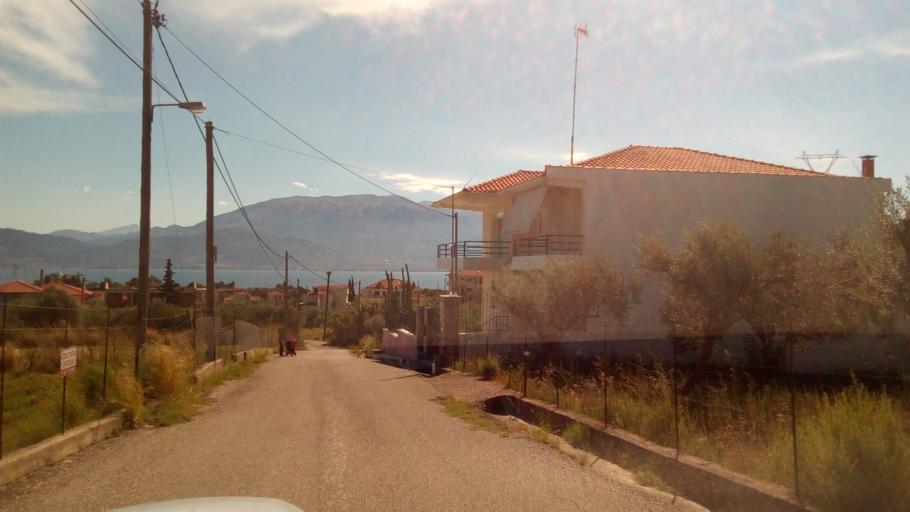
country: GR
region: West Greece
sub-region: Nomos Aitolias kai Akarnanias
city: Antirrio
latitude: 38.3712
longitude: 21.7726
